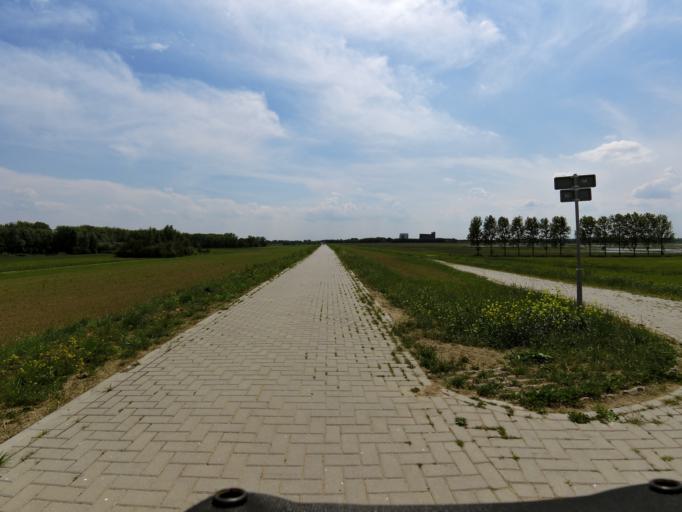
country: NL
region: North Brabant
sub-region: Gemeente Woudrichem
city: Woudrichem
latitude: 51.8104
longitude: 5.0564
